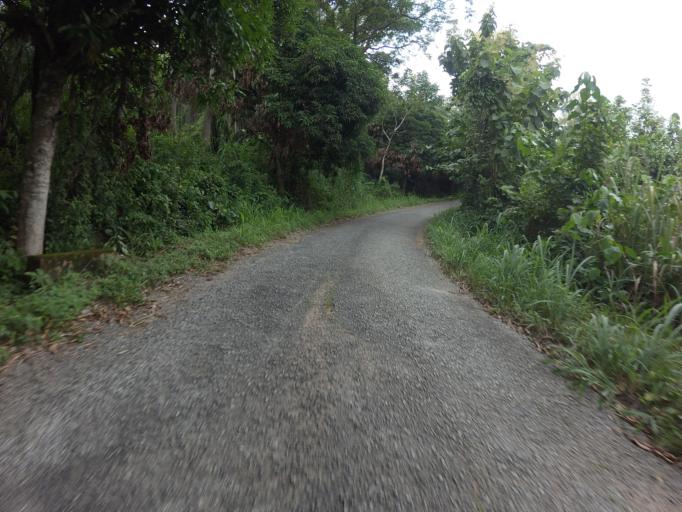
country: GH
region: Volta
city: Kpandu
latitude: 6.8799
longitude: 0.4435
